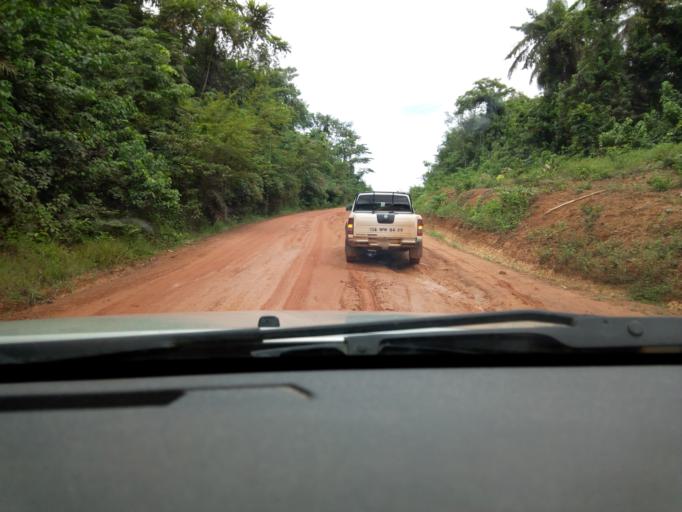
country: CI
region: Dix-Huit Montagnes
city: Toulepleu Guere
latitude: 6.7965
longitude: -8.7966
